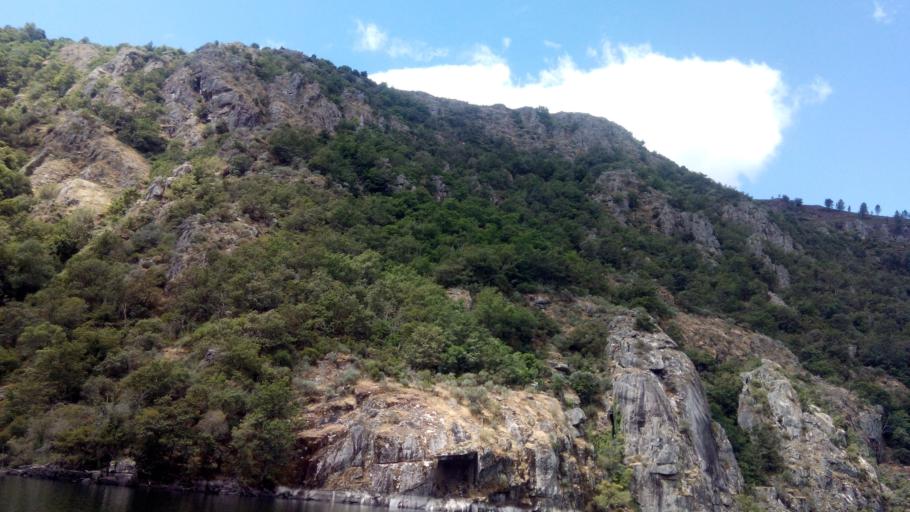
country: ES
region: Galicia
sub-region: Provincia de Lugo
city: Sober
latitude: 42.3938
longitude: -7.6251
